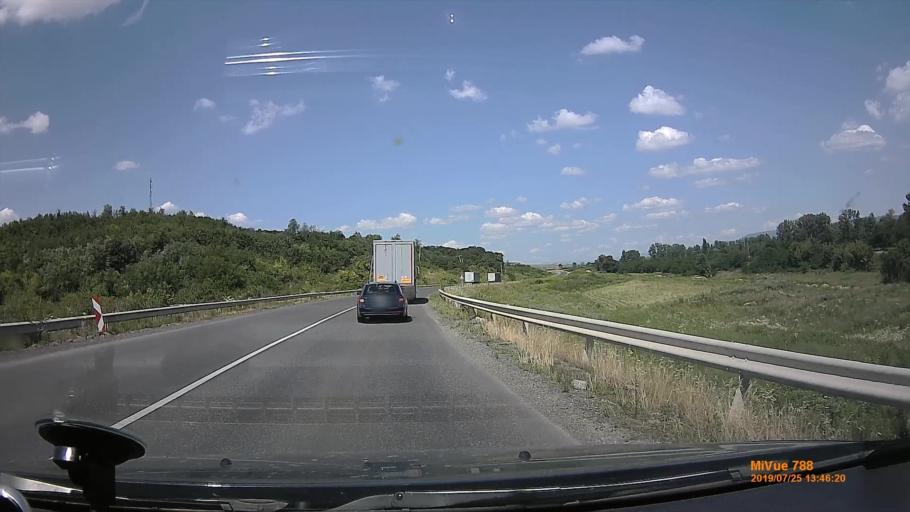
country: HU
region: Borsod-Abauj-Zemplen
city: Gonc
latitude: 48.4865
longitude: 21.2116
